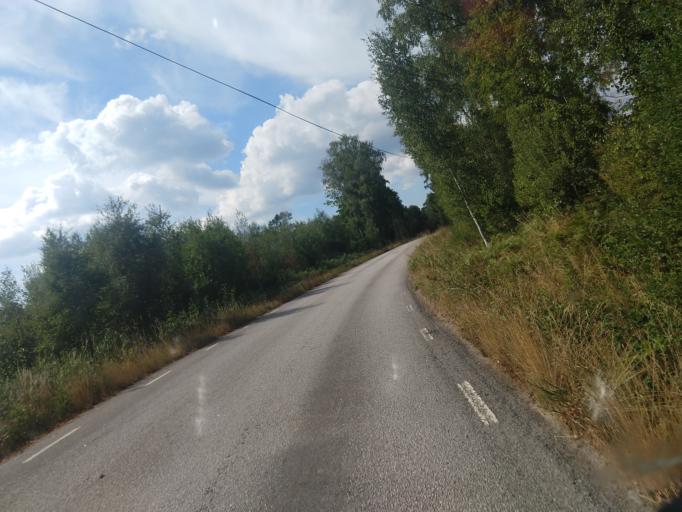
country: SE
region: Blekinge
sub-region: Karlskrona Kommun
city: Rodeby
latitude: 56.2388
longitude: 15.5672
